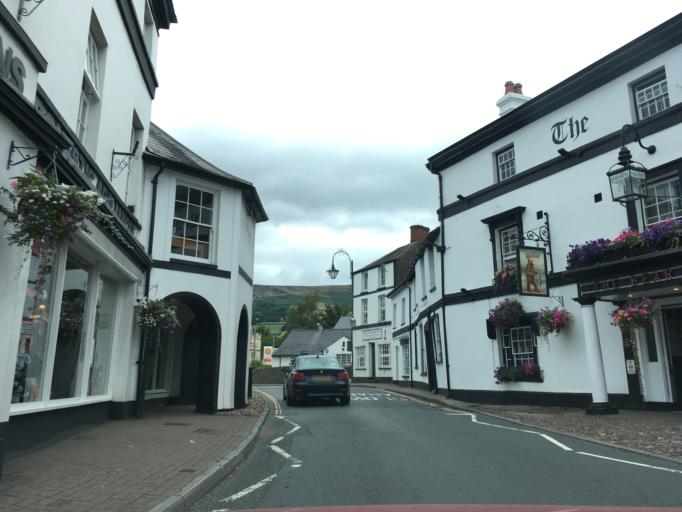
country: GB
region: Wales
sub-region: Monmouthshire
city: Gilwern
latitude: 51.8591
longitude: -3.1371
